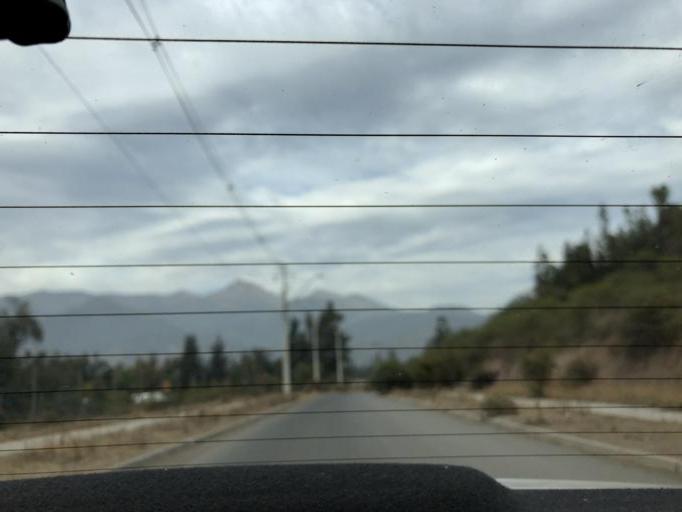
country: CL
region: Santiago Metropolitan
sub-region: Provincia de Cordillera
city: Puente Alto
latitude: -33.5910
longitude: -70.5198
